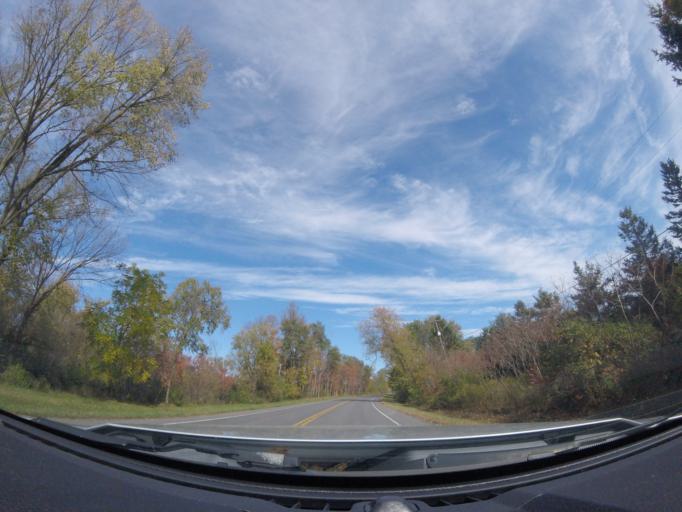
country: US
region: New York
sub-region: Tompkins County
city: Dryden
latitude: 42.5244
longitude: -76.3237
